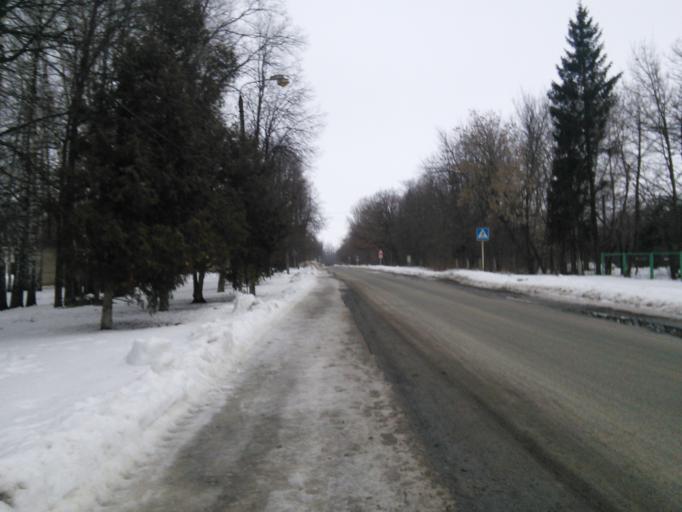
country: RU
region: Kursk
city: Chernitsyno
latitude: 51.5690
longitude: 36.0856
